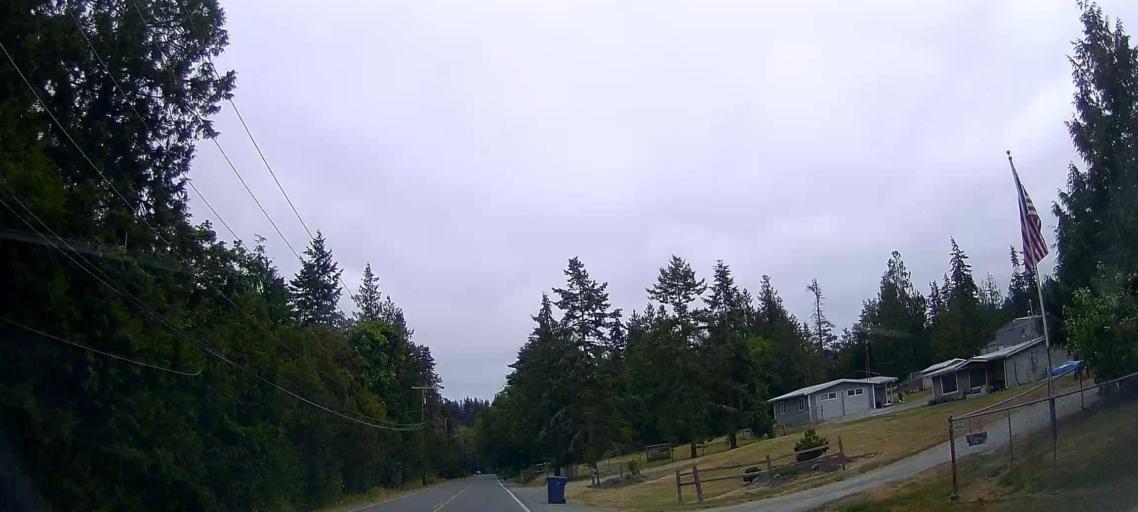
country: US
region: Washington
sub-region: Skagit County
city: Anacortes
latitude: 48.4507
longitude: -122.6459
